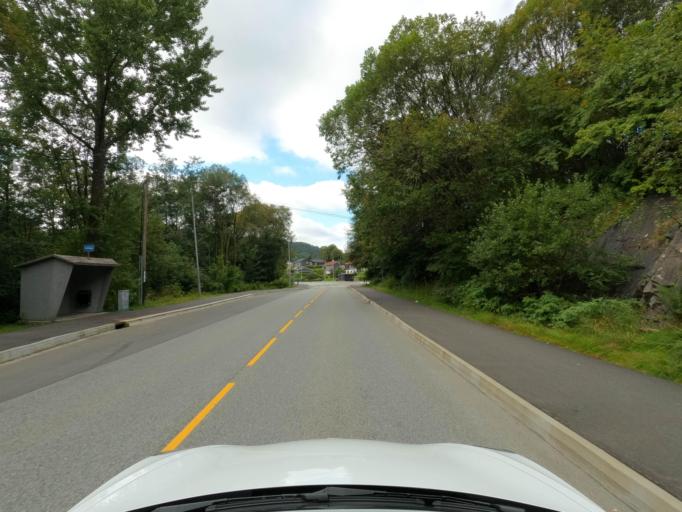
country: NO
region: Hordaland
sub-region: Bergen
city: Sandsli
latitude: 60.3099
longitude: 5.3740
